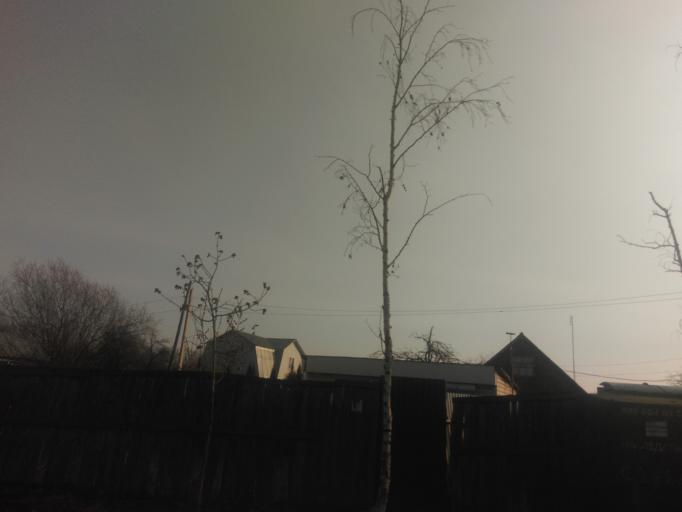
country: RU
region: Moskovskaya
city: Kokoshkino
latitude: 55.5813
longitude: 37.1248
